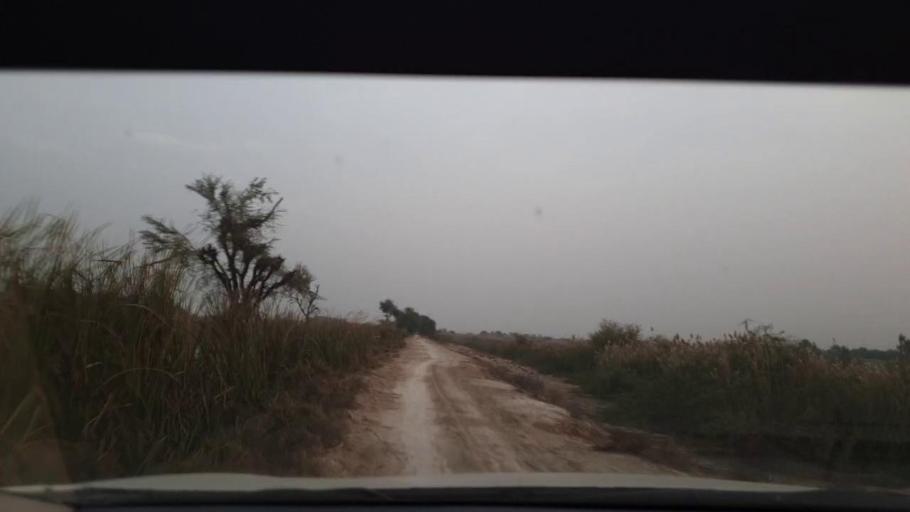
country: PK
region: Sindh
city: Berani
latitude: 25.8515
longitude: 68.7827
